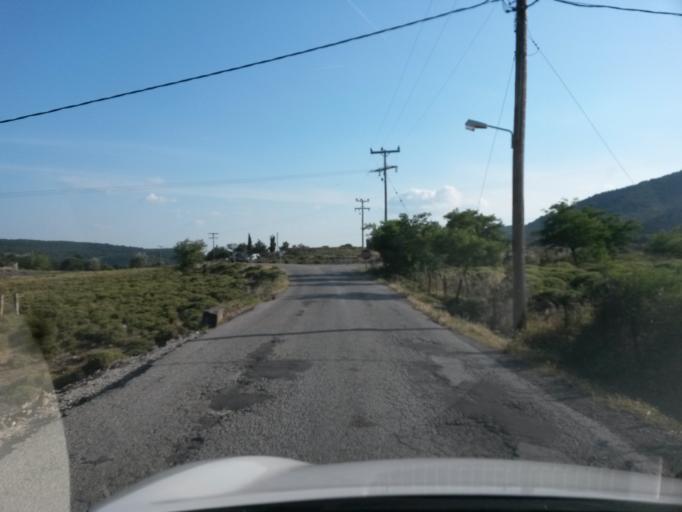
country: GR
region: North Aegean
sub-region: Nomos Lesvou
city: Mantamados
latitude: 39.3429
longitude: 26.3193
